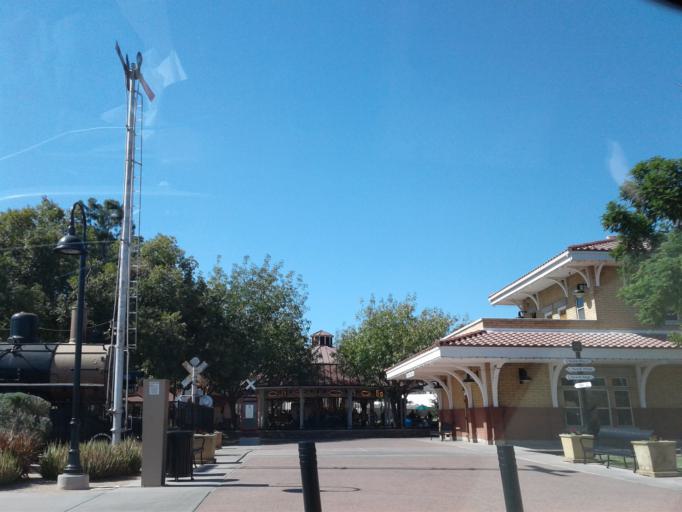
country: US
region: Arizona
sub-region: Maricopa County
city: Paradise Valley
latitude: 33.5375
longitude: -111.9227
